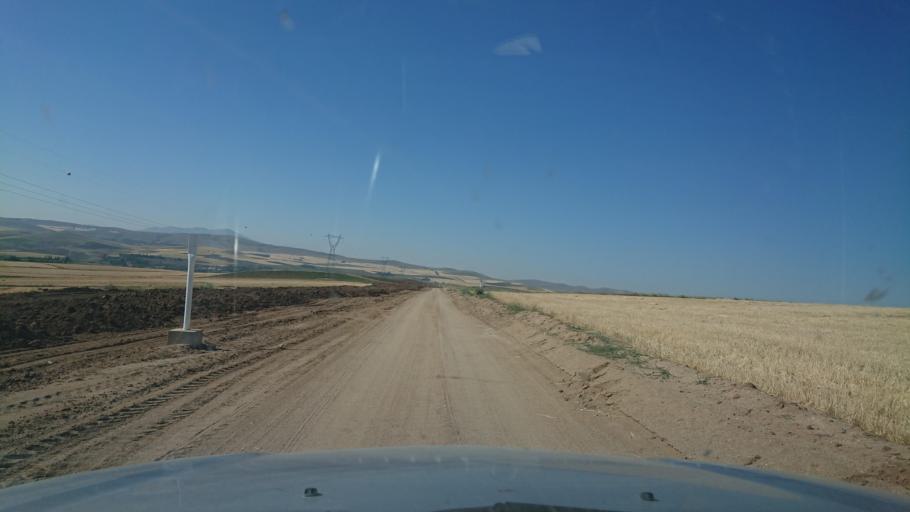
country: TR
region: Aksaray
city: Agacoren
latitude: 38.8405
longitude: 33.9442
